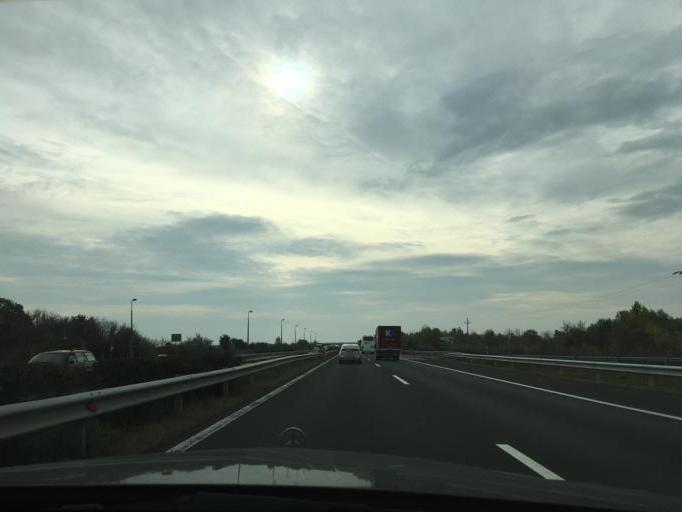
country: HU
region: Gyor-Moson-Sopron
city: Mosonmagyarovar
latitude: 47.8710
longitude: 17.2169
